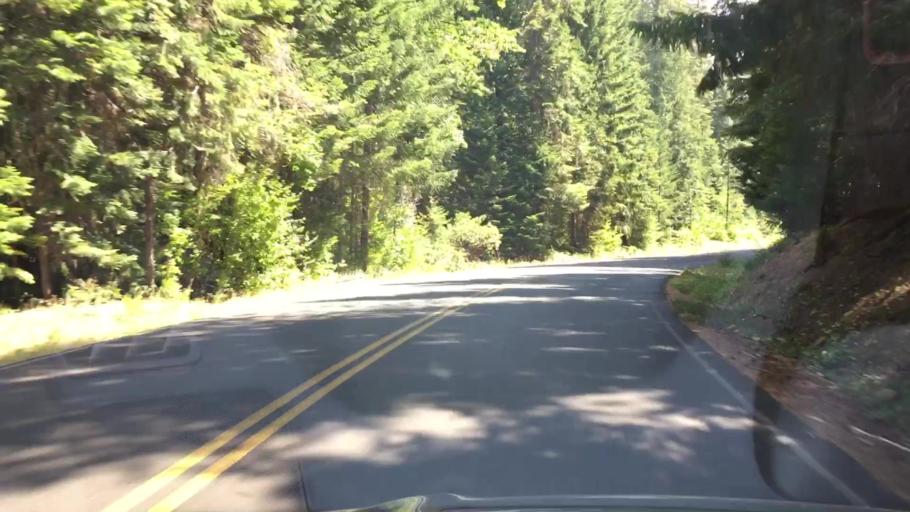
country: US
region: Washington
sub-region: Klickitat County
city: White Salmon
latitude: 46.0654
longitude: -121.5722
